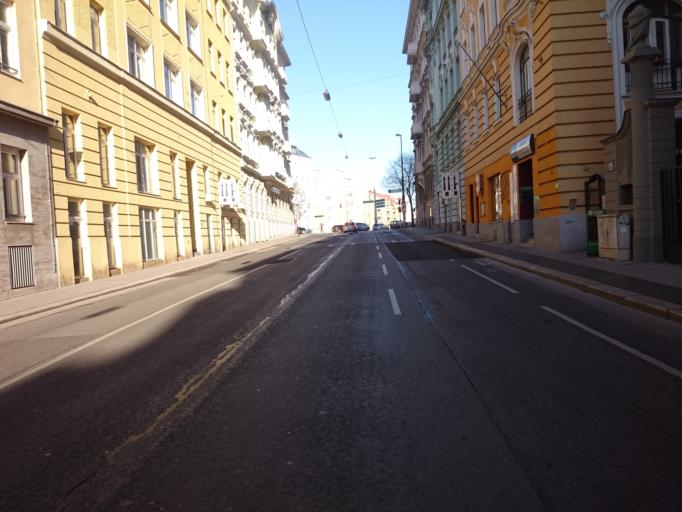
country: AT
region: Vienna
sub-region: Wien Stadt
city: Vienna
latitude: 48.2319
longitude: 16.3561
